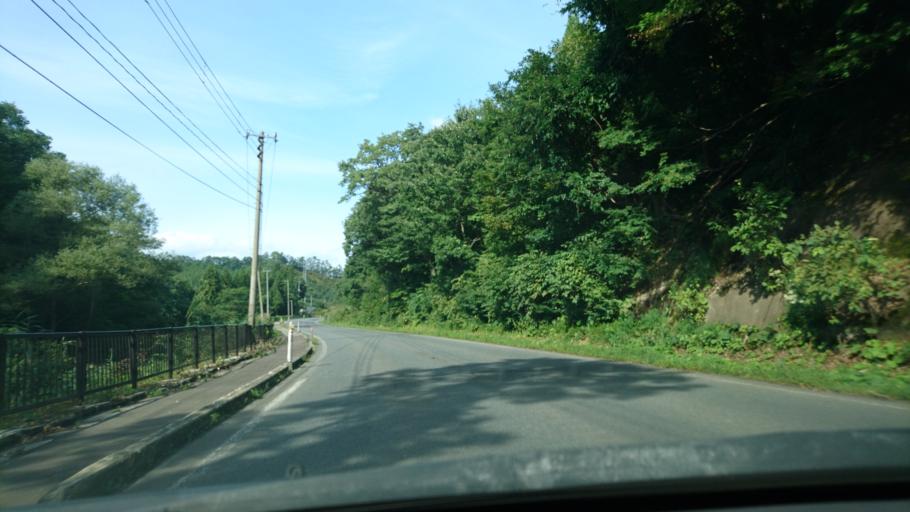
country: JP
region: Akita
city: Yokotemachi
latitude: 39.3124
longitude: 140.7502
